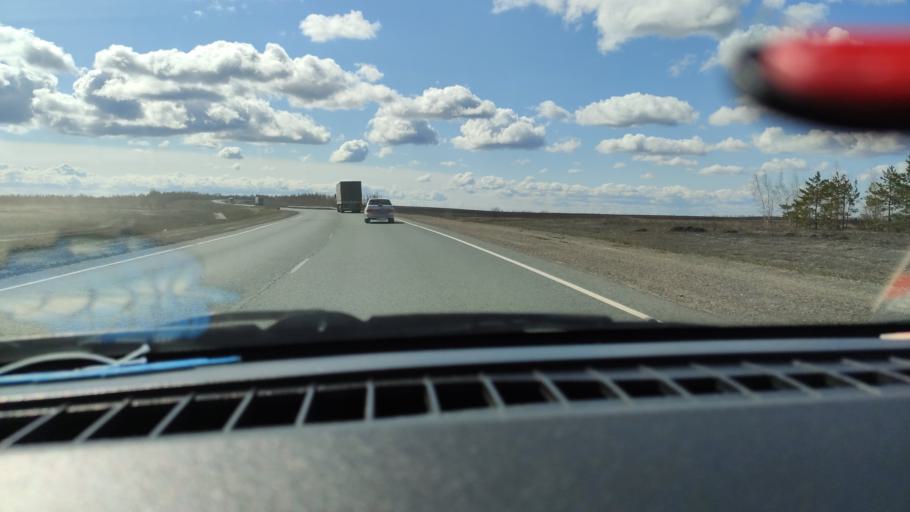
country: RU
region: Samara
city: Syzran'
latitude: 52.9399
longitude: 48.3059
